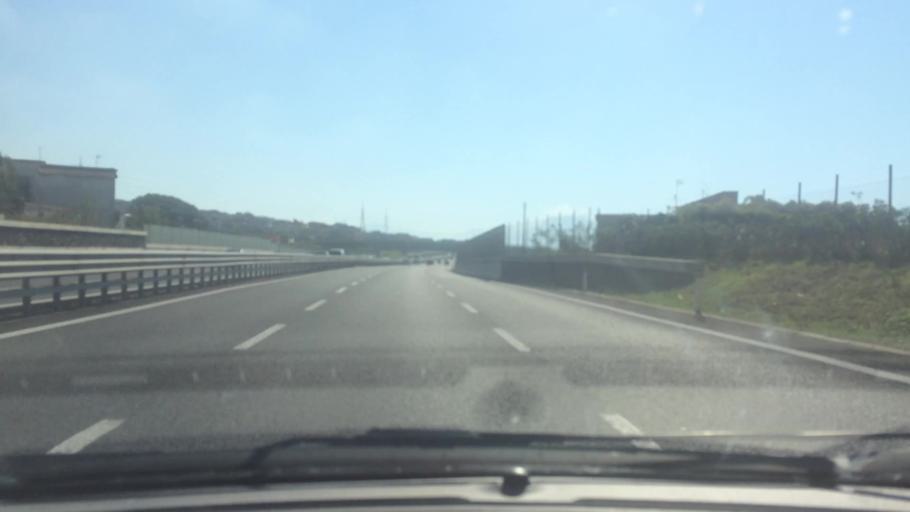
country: IT
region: Campania
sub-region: Provincia di Napoli
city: Ercolano
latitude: 40.8128
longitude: 14.3587
